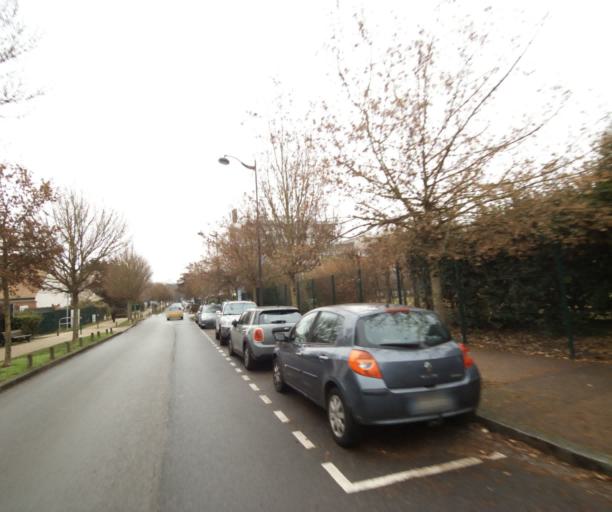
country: FR
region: Ile-de-France
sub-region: Departement des Yvelines
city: Chatou
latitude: 48.8760
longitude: 2.1638
